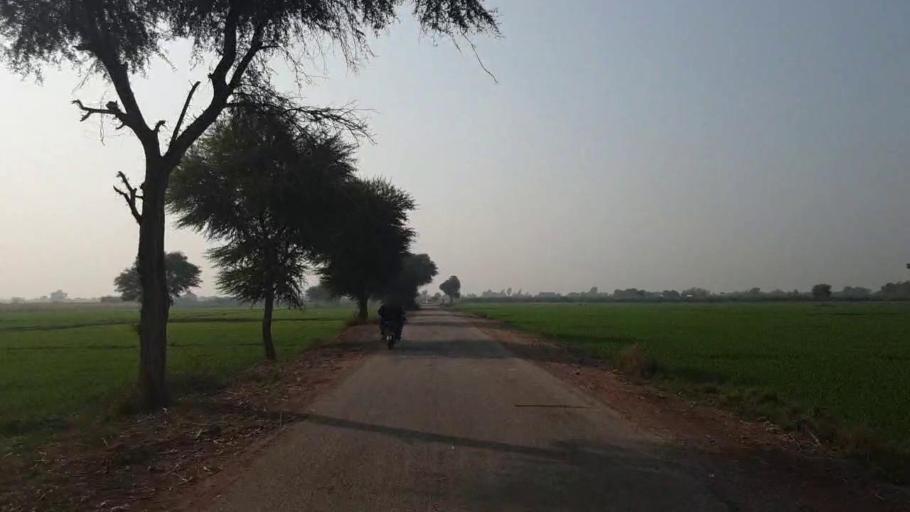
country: PK
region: Sindh
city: Shahdadpur
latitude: 25.9710
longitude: 68.5480
